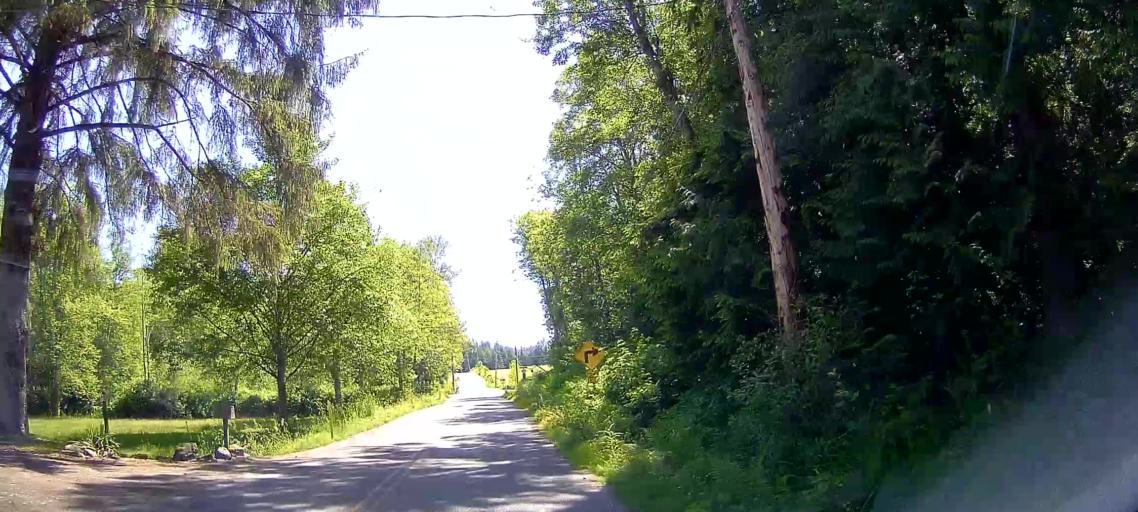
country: US
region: Washington
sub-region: Skagit County
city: Sedro-Woolley
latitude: 48.5576
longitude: -122.2481
